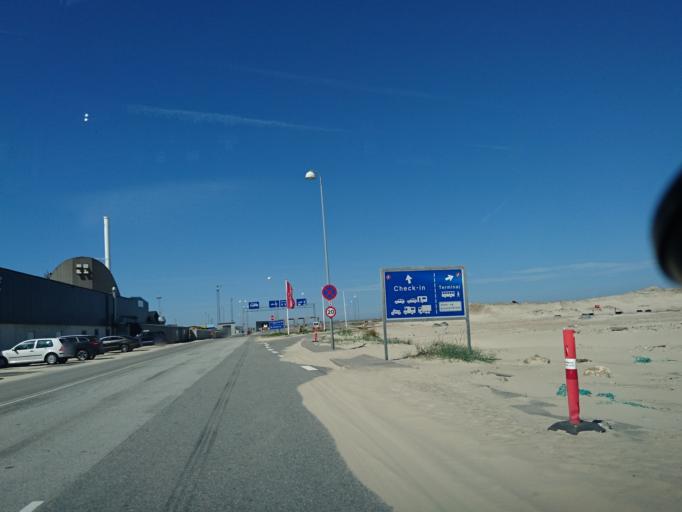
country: DK
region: North Denmark
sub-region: Hjorring Kommune
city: Hirtshals
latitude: 57.5932
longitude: 9.9838
